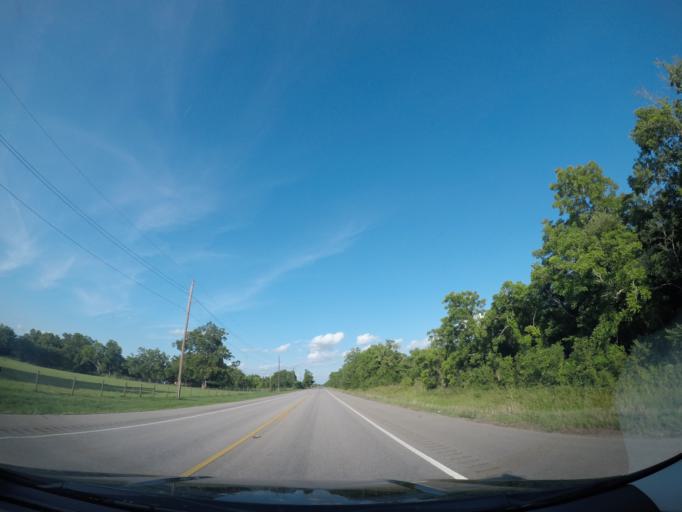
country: US
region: Texas
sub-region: Fort Bend County
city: Weston Lakes
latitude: 29.6771
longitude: -96.0023
